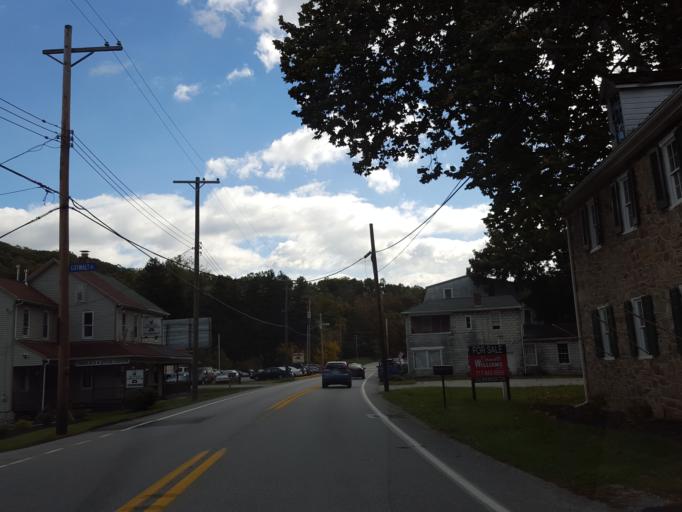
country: US
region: Pennsylvania
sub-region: York County
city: Grantley
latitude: 39.9375
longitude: -76.7156
